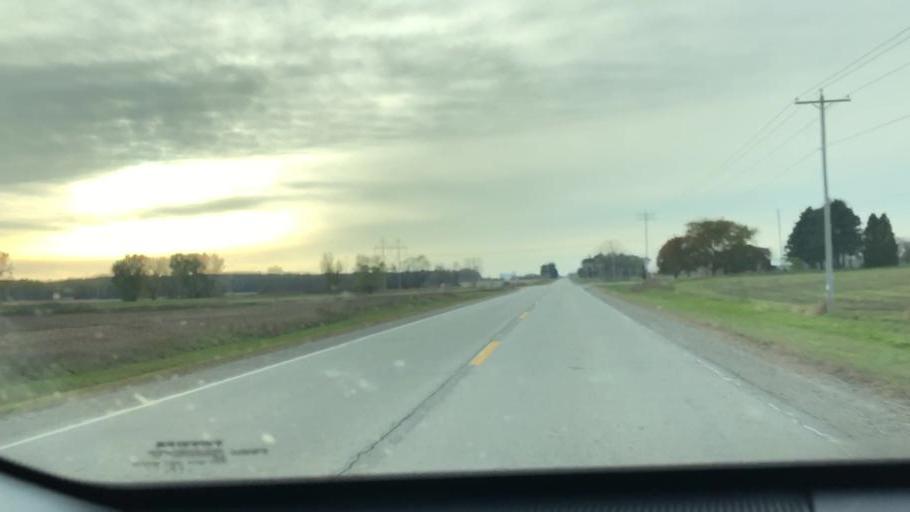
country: US
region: Wisconsin
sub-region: Outagamie County
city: Seymour
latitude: 44.4437
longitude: -88.3097
